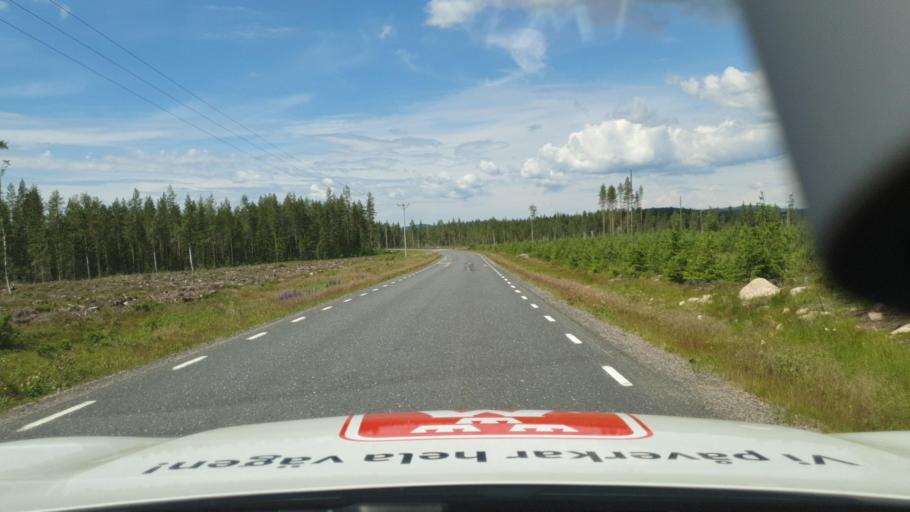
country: SE
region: Vaermland
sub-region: Torsby Kommun
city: Torsby
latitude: 60.5065
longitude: 12.8492
